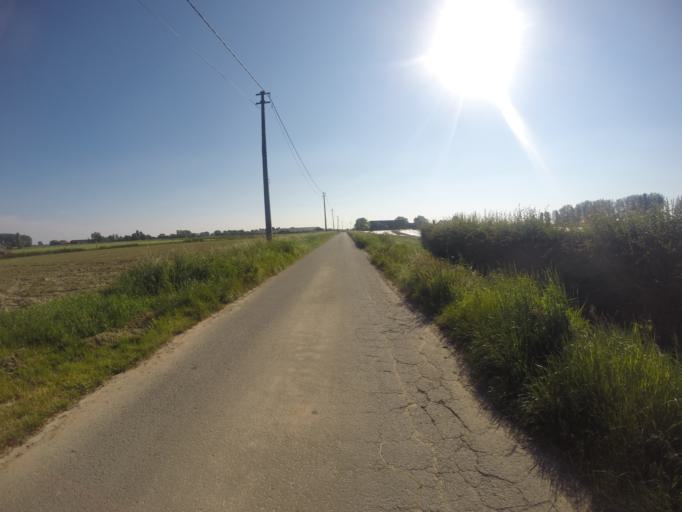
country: BE
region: Flanders
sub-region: Provincie West-Vlaanderen
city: Ruiselede
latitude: 51.0490
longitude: 3.4285
